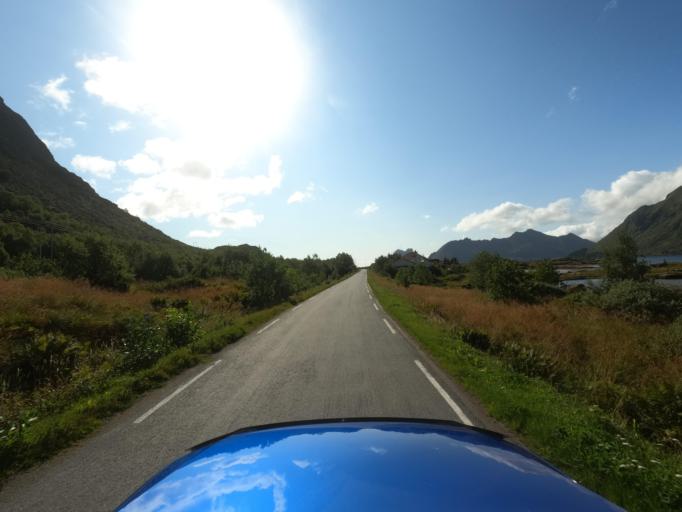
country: NO
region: Nordland
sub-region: Vestvagoy
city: Evjen
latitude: 68.1336
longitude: 13.7811
